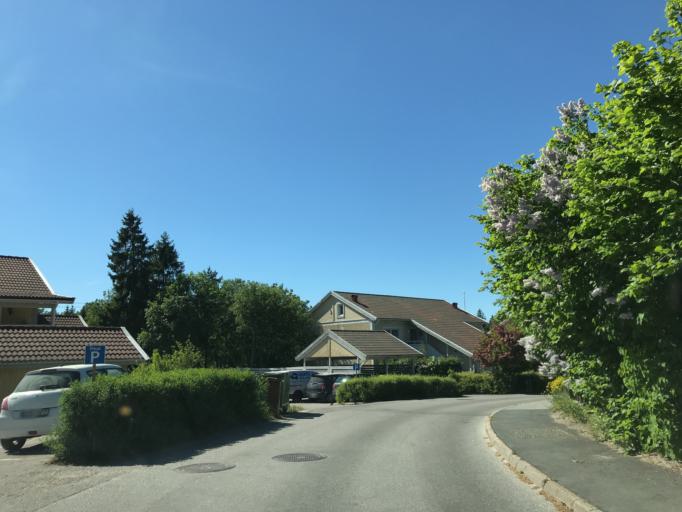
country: SE
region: Stockholm
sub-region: Sollentuna Kommun
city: Sollentuna
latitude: 59.4512
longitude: 17.8920
